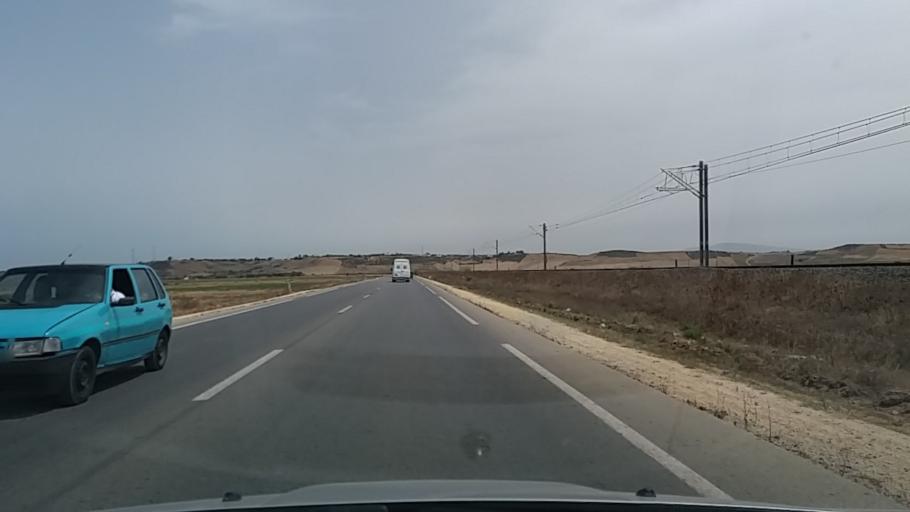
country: MA
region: Tanger-Tetouan
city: Asilah
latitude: 35.5010
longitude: -6.0082
